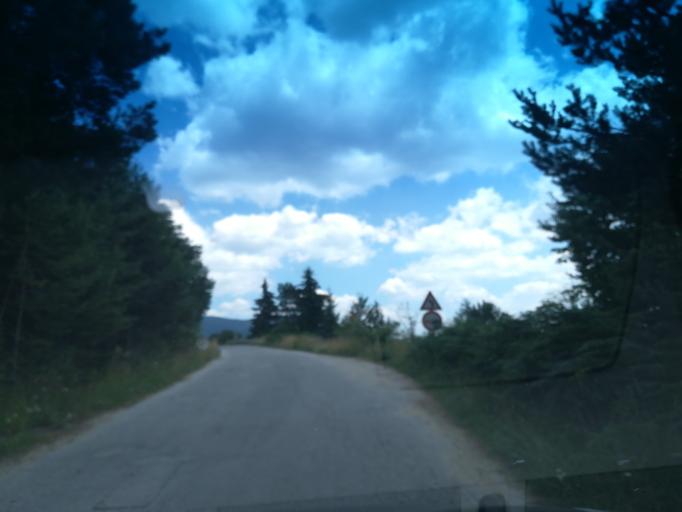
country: BG
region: Smolyan
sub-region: Obshtina Chepelare
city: Chepelare
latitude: 41.6730
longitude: 24.7807
